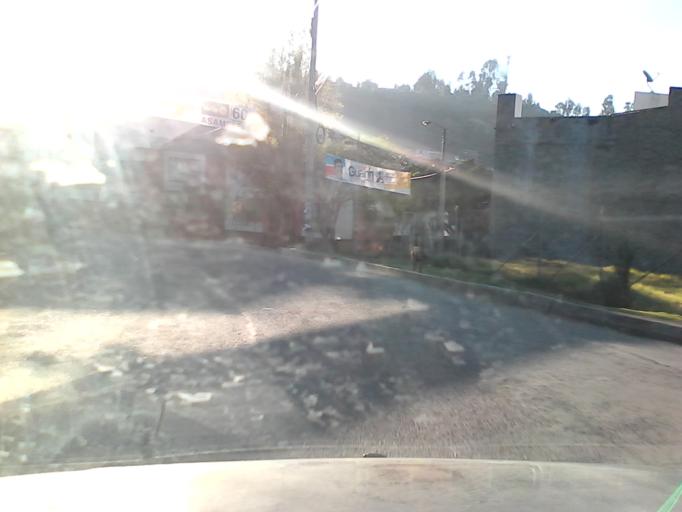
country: CO
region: Boyaca
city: Duitama
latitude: 5.8334
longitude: -73.0313
